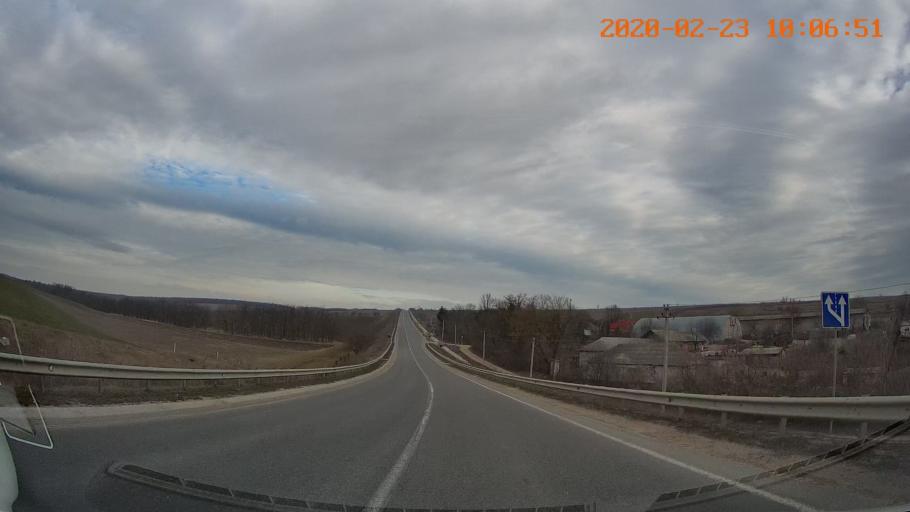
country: MD
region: Soldanesti
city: Soldanesti
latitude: 47.7045
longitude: 28.8455
